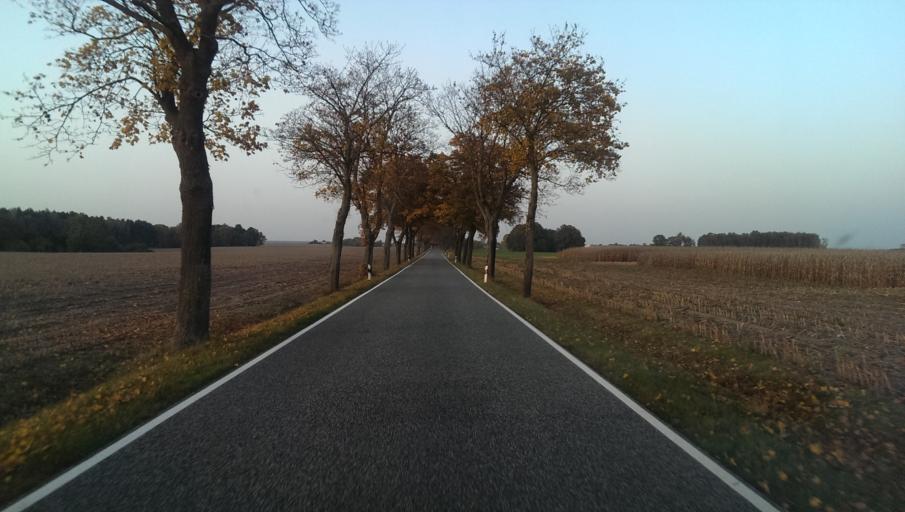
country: DE
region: Brandenburg
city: Niedergorsdorf
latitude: 51.9146
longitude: 13.0277
